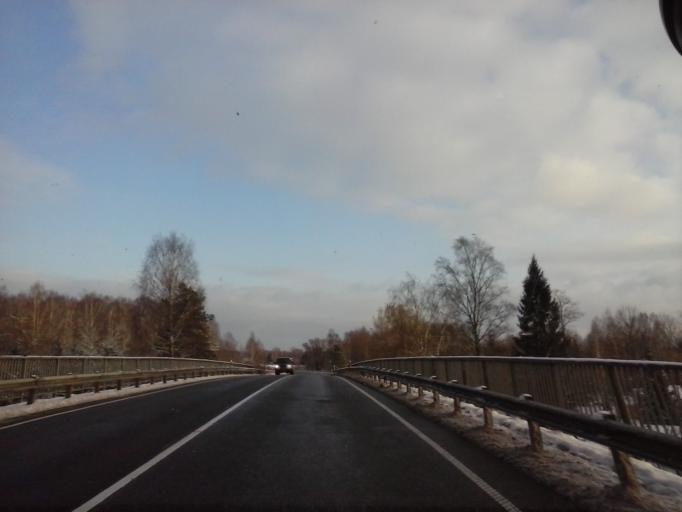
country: EE
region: Tartu
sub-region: Tartu linn
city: Tartu
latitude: 58.3569
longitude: 26.9017
